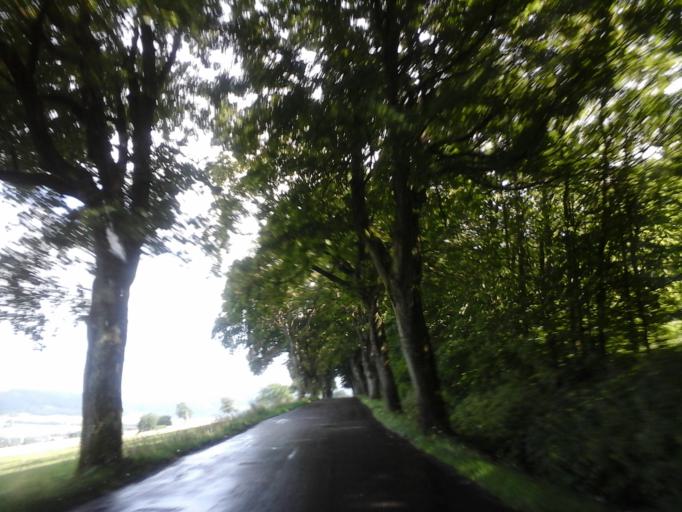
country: CZ
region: Pardubicky
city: Cervena Voda
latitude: 50.0549
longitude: 16.7187
